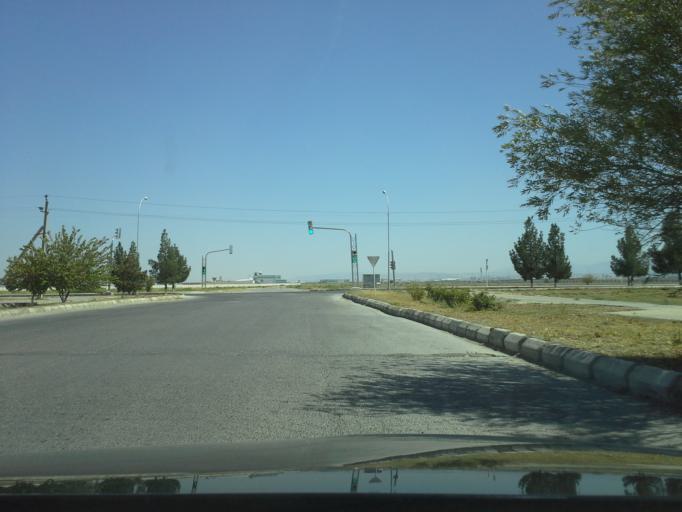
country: TM
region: Ahal
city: Ashgabat
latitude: 38.0026
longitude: 58.3293
